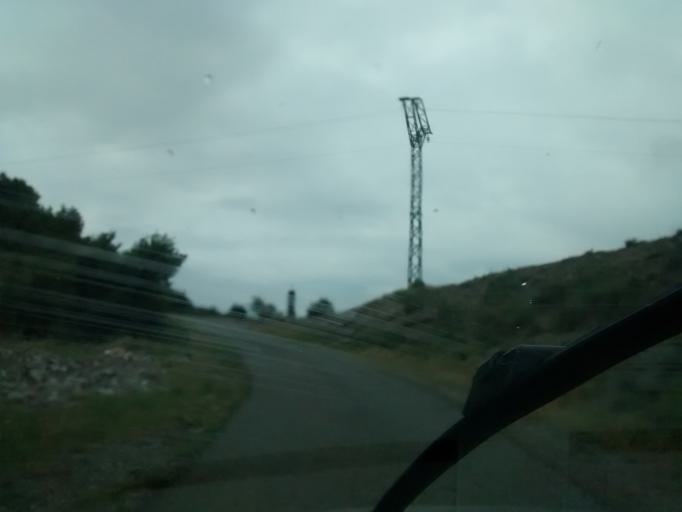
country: ES
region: Aragon
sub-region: Provincia de Huesca
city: Puertolas
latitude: 42.5511
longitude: 0.1328
